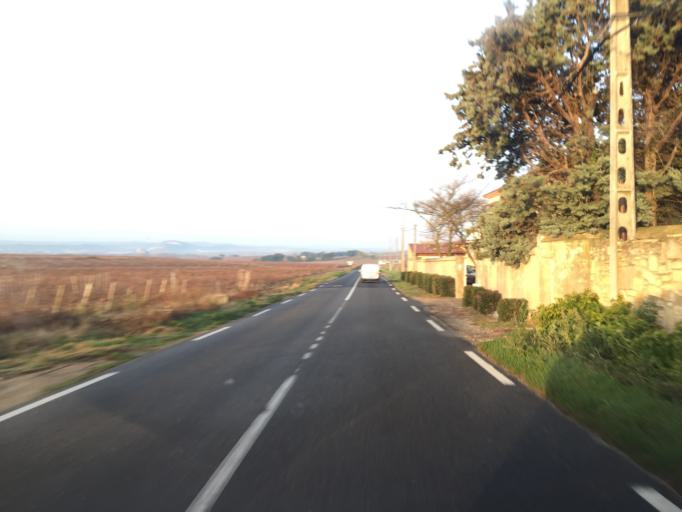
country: FR
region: Provence-Alpes-Cote d'Azur
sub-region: Departement du Vaucluse
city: Chateauneuf-du-Pape
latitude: 44.0566
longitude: 4.8227
